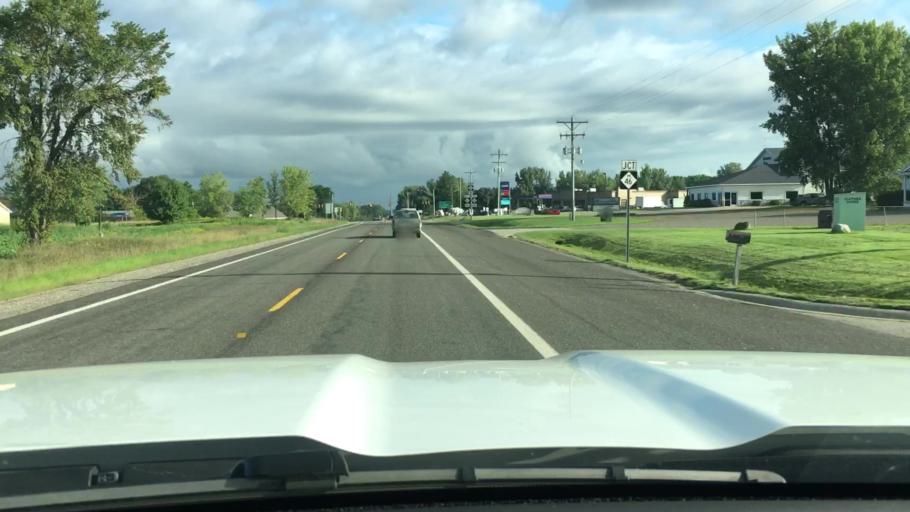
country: US
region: Michigan
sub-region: Tuscola County
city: Caro
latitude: 43.4062
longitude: -83.3837
